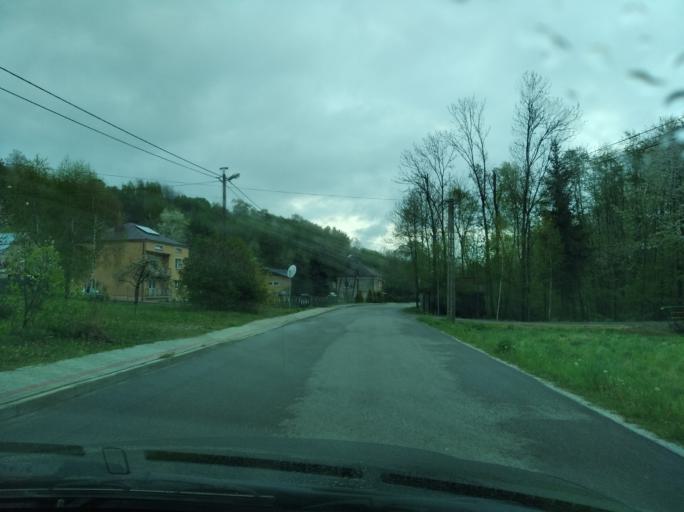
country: PL
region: Subcarpathian Voivodeship
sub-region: Powiat rzeszowski
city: Lecka
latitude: 49.8773
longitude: 22.0174
